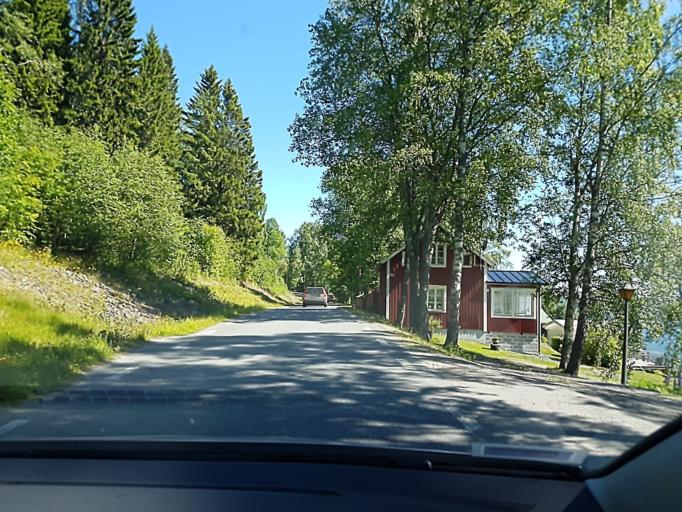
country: SE
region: Vaesternorrland
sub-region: Kramfors Kommun
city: Nordingra
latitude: 63.0611
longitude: 18.3950
